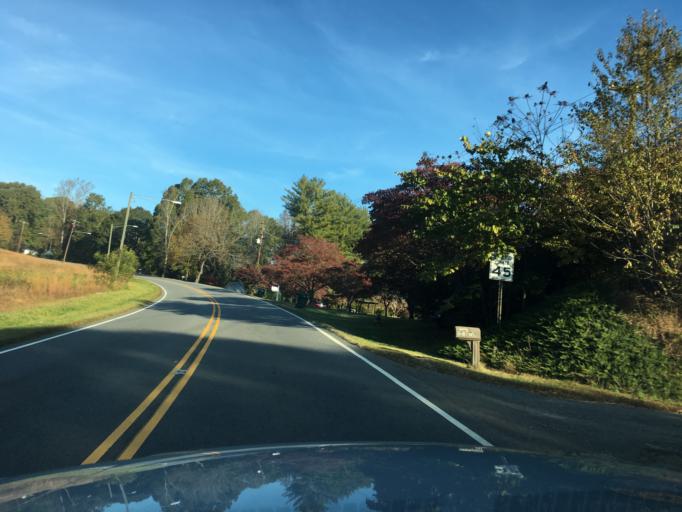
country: US
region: North Carolina
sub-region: Catawba County
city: Newton
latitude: 35.6878
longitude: -81.2540
